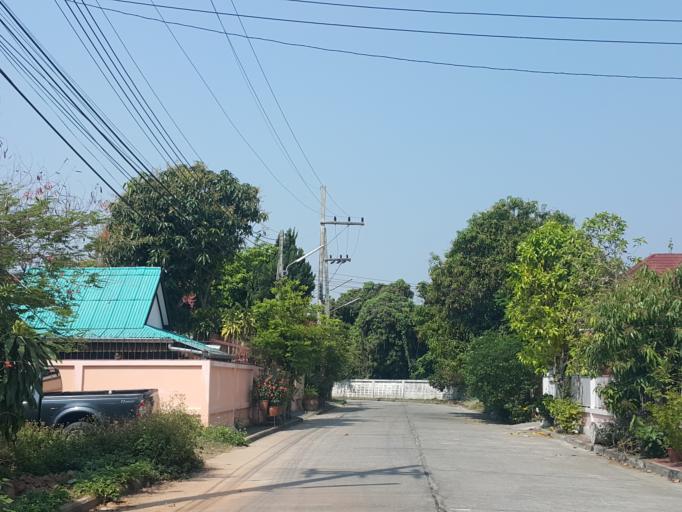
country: TH
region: Chiang Mai
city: San Kamphaeng
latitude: 18.7401
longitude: 99.1156
